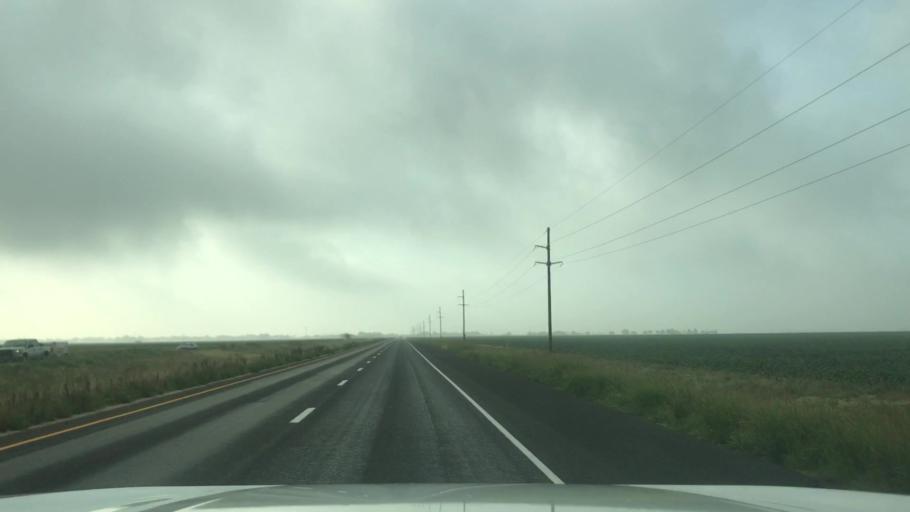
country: US
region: Texas
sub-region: Lubbock County
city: Slaton
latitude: 33.3708
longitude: -101.5720
